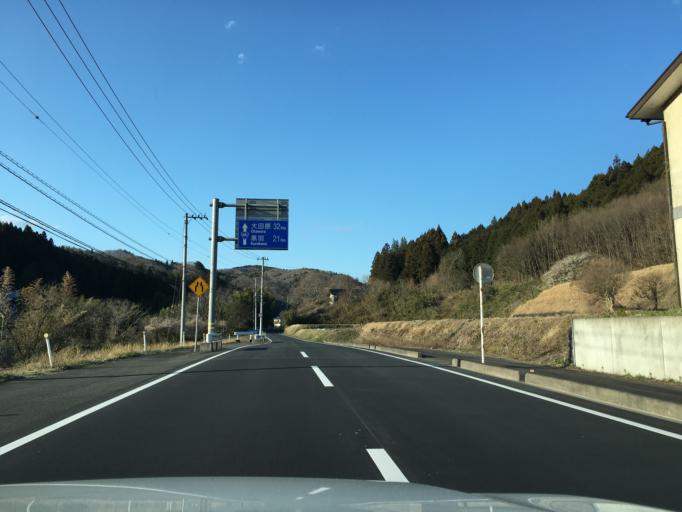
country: JP
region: Tochigi
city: Karasuyama
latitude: 36.7585
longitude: 140.2022
